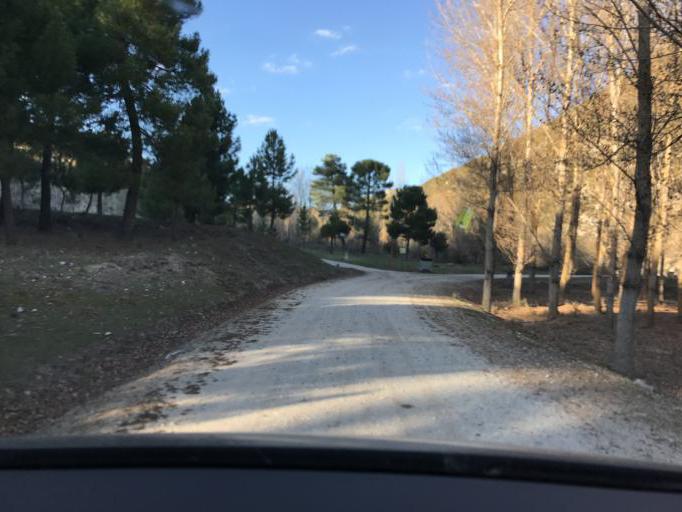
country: ES
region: Andalusia
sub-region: Provincia de Granada
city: Quentar
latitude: 37.2358
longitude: -3.4060
